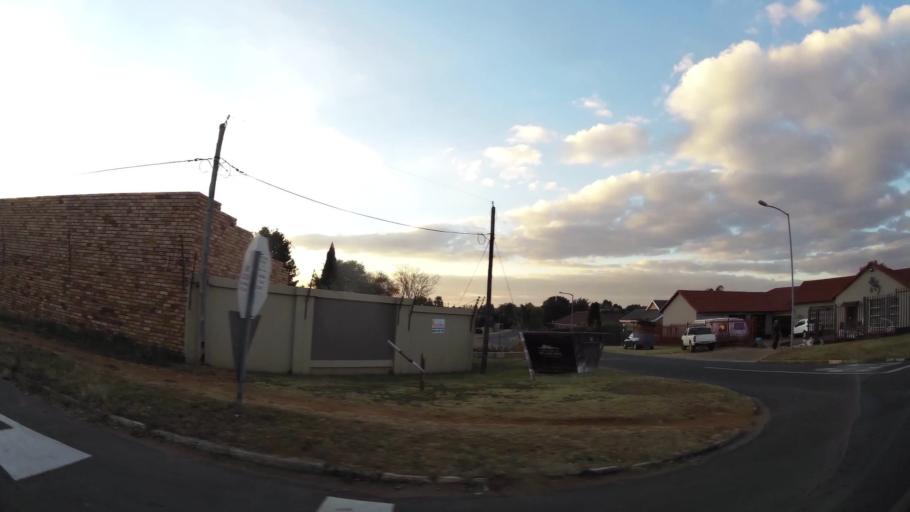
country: ZA
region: Gauteng
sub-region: West Rand District Municipality
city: Krugersdorp
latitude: -26.0760
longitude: 27.7836
